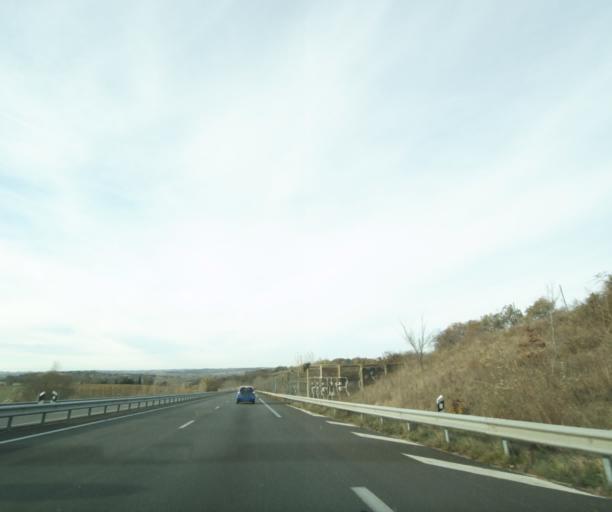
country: FR
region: Midi-Pyrenees
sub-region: Departement du Gers
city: Pujaudran
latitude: 43.5969
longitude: 1.1104
